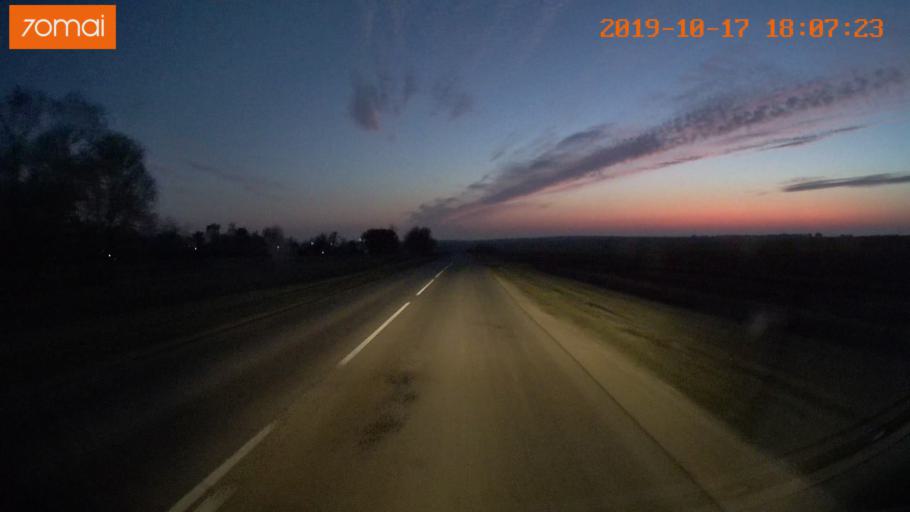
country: RU
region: Tula
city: Kurkino
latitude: 53.4448
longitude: 38.6562
